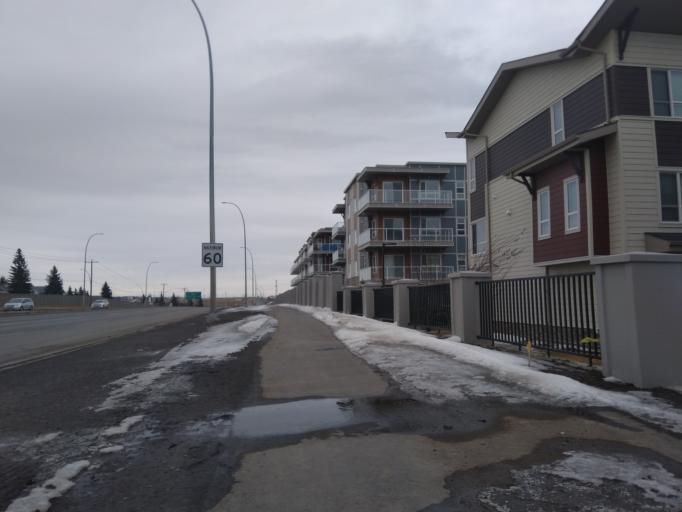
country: CA
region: Alberta
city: Calgary
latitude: 51.1542
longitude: -114.0460
